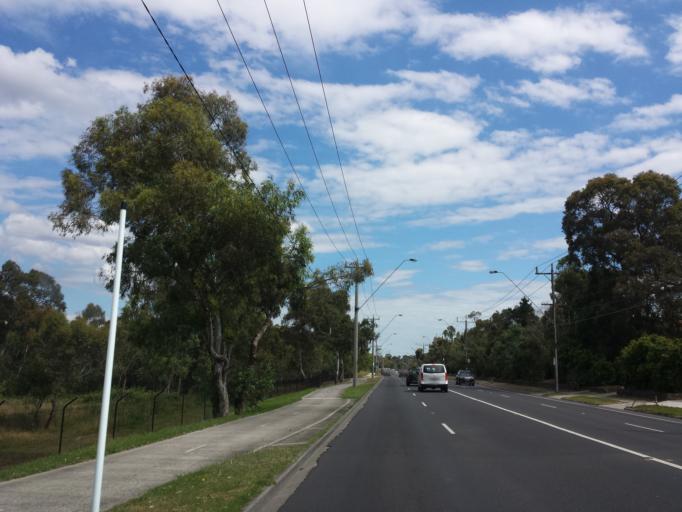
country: AU
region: Victoria
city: Watsonia
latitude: -37.7275
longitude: 145.0799
